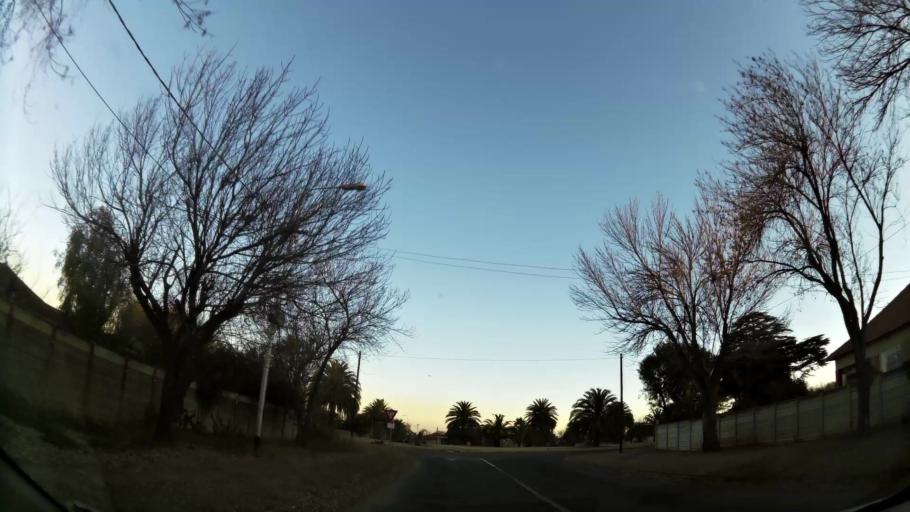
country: ZA
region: Gauteng
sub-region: City of Johannesburg Metropolitan Municipality
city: Roodepoort
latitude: -26.1601
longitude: 27.8969
